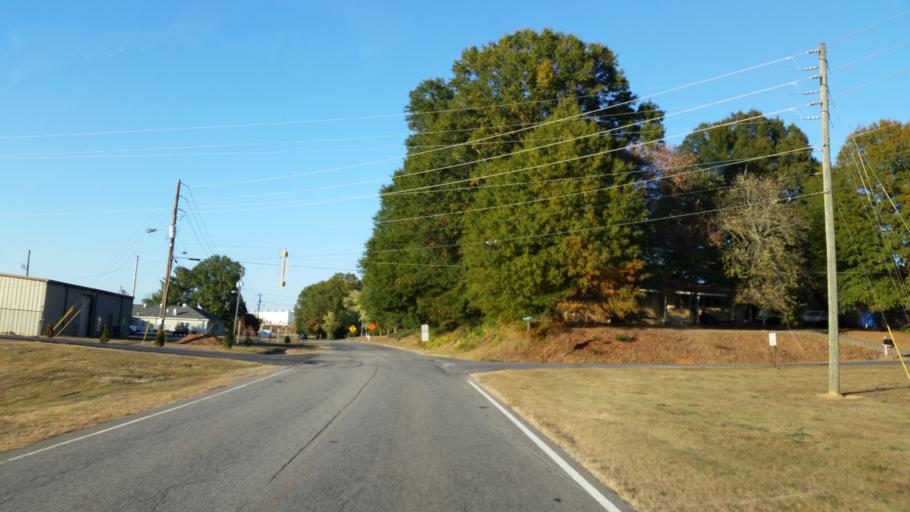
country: US
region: Georgia
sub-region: Bartow County
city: Adairsville
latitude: 34.3730
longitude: -84.9405
